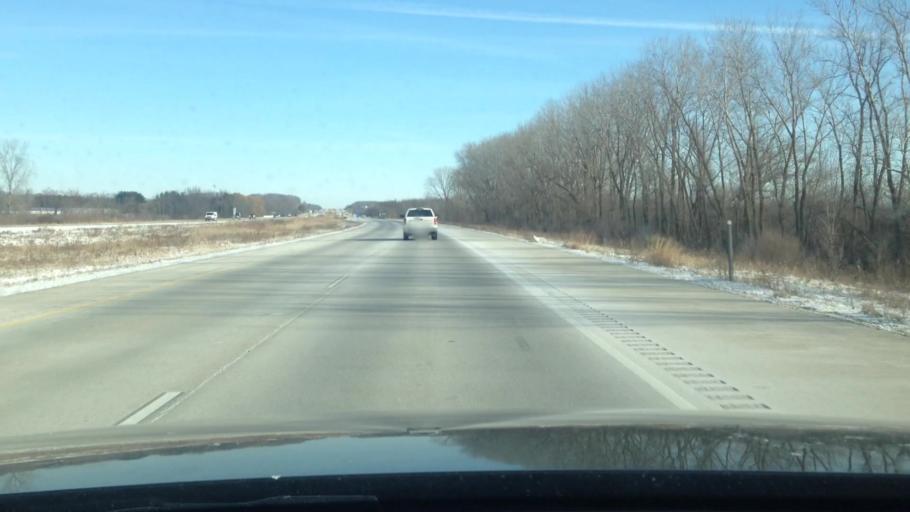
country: US
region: Wisconsin
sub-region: Waukesha County
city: Mukwonago
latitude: 42.8645
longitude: -88.3006
